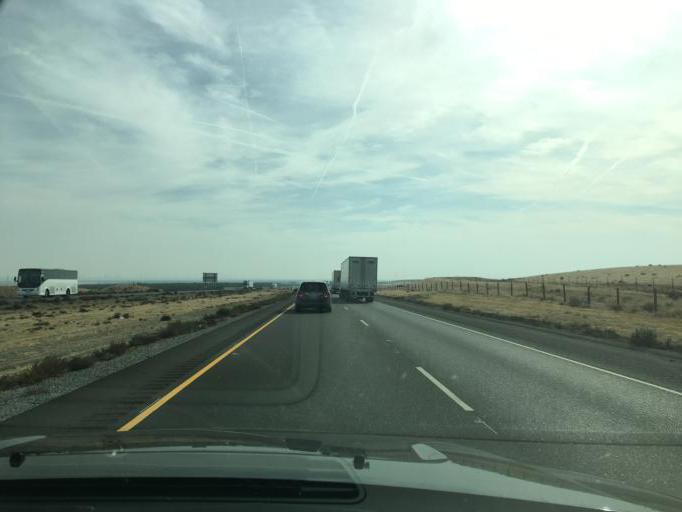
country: US
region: California
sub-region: Kings County
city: Kettleman City
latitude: 35.9654
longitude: -119.9438
